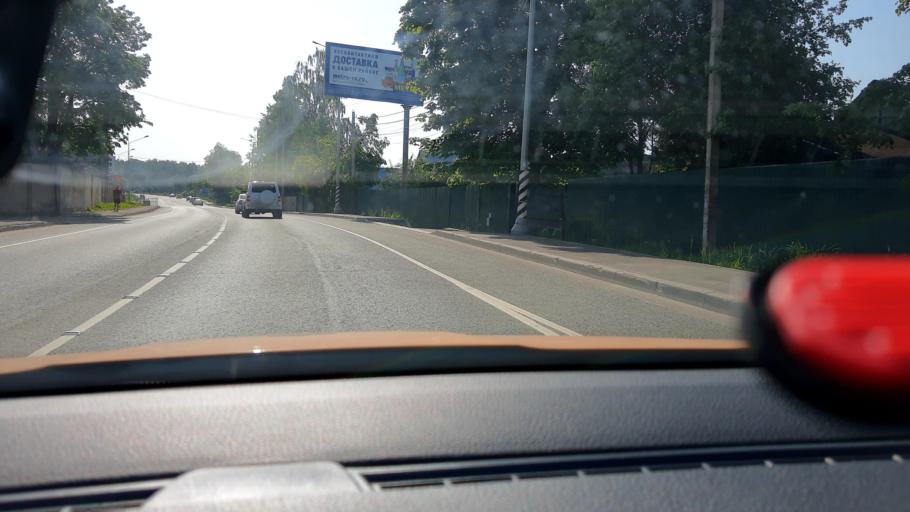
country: RU
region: Moskovskaya
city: Rozhdestveno
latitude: 55.8096
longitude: 37.0151
